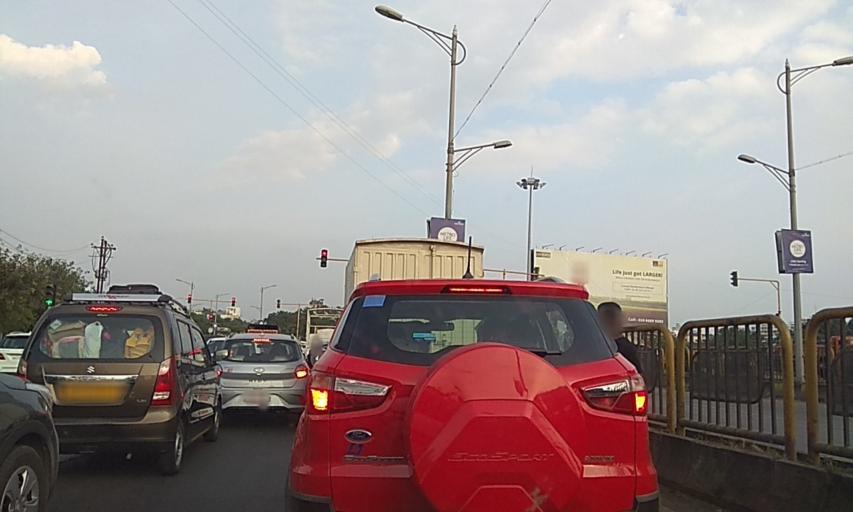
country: IN
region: Maharashtra
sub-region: Pune Division
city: Pimpri
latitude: 18.5891
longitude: 73.7764
